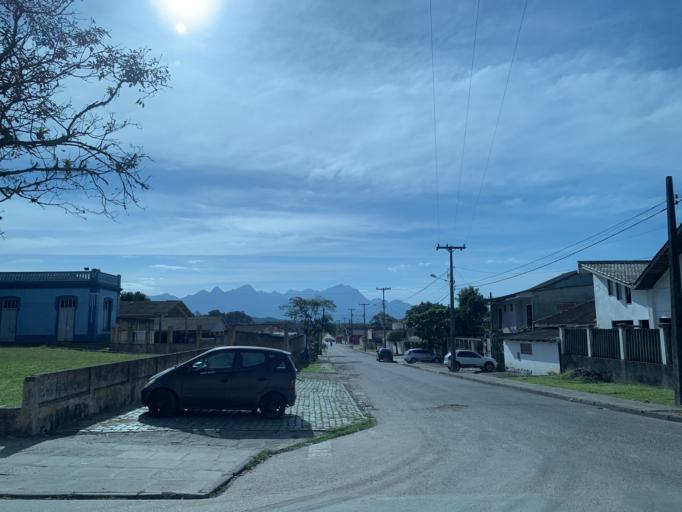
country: BR
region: Parana
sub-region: Antonina
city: Antonina
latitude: -25.4341
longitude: -48.7267
